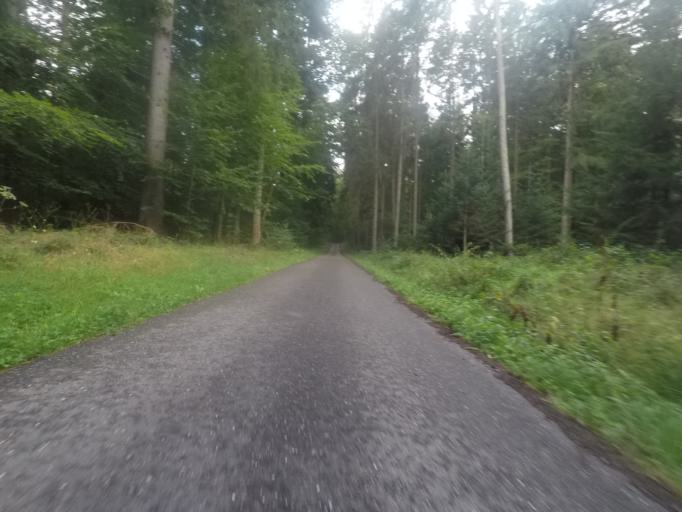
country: DE
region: Baden-Wuerttemberg
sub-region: Karlsruhe Region
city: Ettlingen
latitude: 48.8907
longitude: 8.4032
